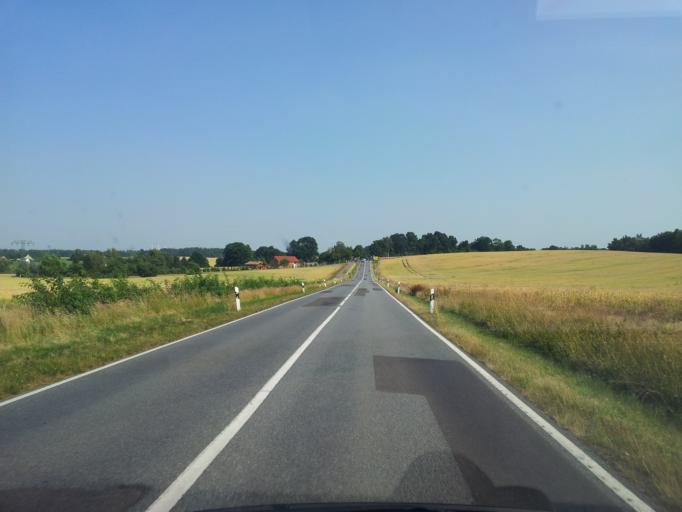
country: DE
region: Saxony
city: Wachau
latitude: 51.1505
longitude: 13.8970
